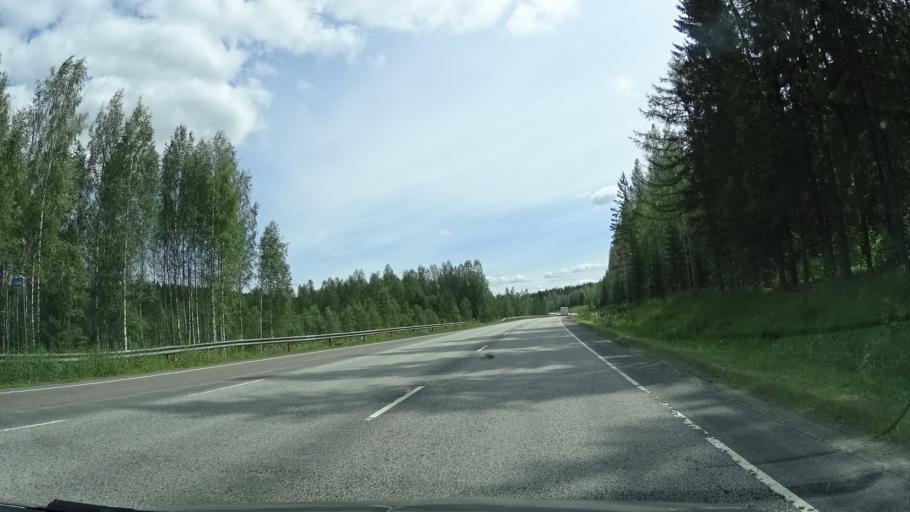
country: FI
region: Central Finland
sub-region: Jyvaeskylae
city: Jyvaeskylae
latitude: 62.2560
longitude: 25.6209
